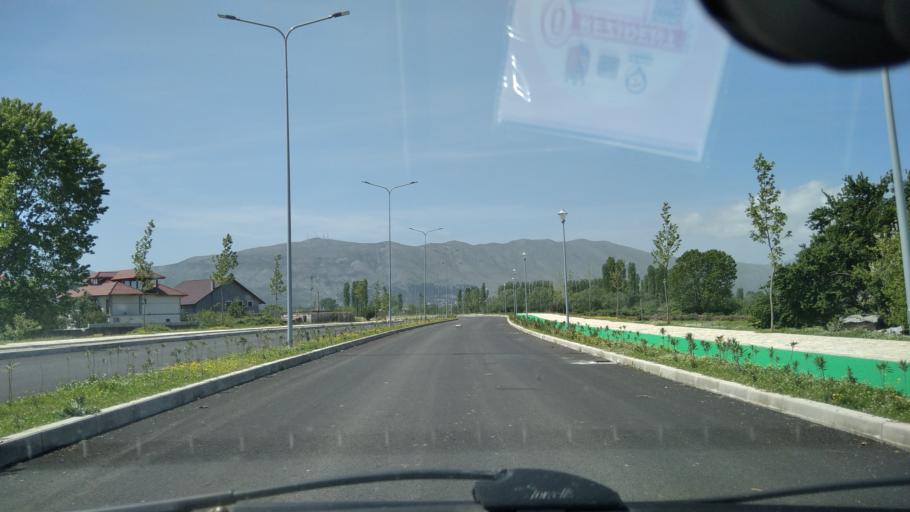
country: AL
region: Shkoder
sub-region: Rrethi i Shkodres
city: Shkoder
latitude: 42.0824
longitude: 19.4946
